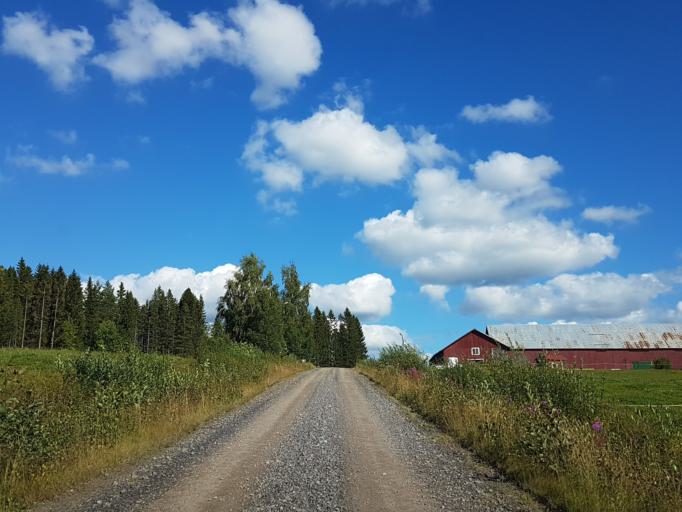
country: SE
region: Vaesterbotten
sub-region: Skelleftea Kommun
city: Burtraesk
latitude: 64.2929
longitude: 20.4613
